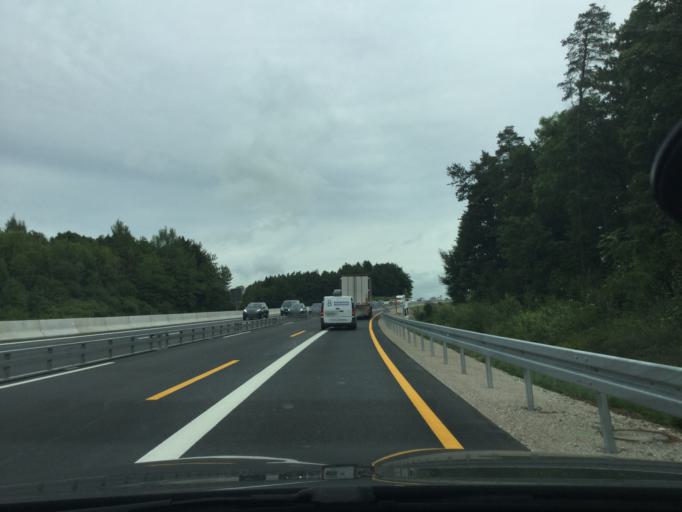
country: DE
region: Bavaria
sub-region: Upper Franconia
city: Pegnitz
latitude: 49.7997
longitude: 11.4935
